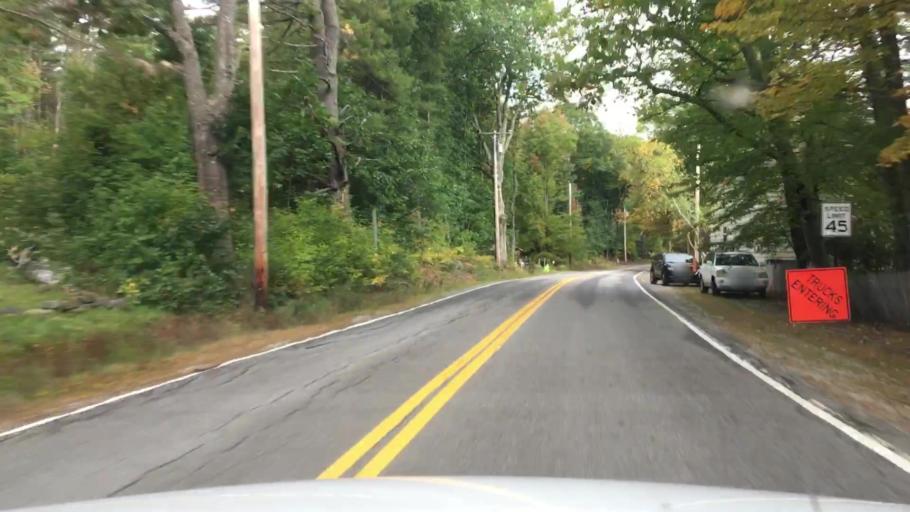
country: US
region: Maine
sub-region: Oxford County
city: Bethel
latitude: 44.3495
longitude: -70.7899
